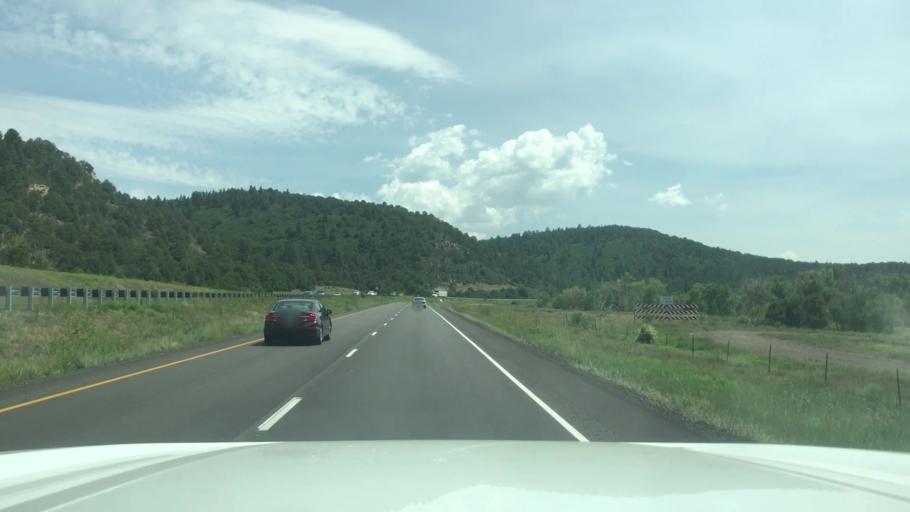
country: US
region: Colorado
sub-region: Las Animas County
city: Trinidad
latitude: 37.0989
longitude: -104.5214
